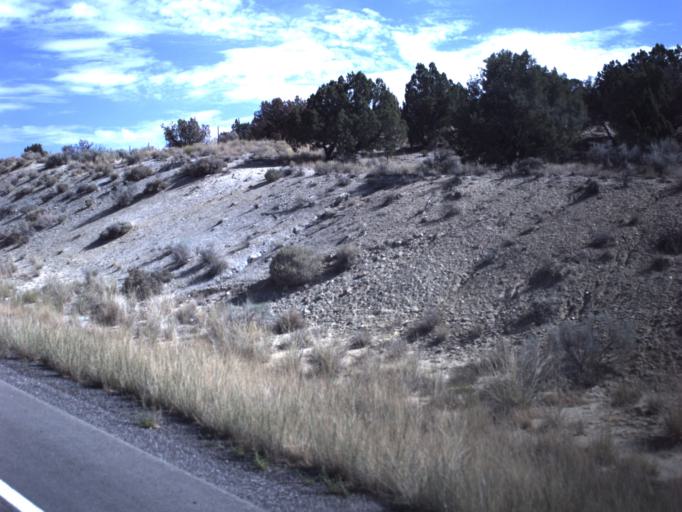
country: US
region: Utah
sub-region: Sanpete County
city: Gunnison
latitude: 39.3878
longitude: -111.9278
